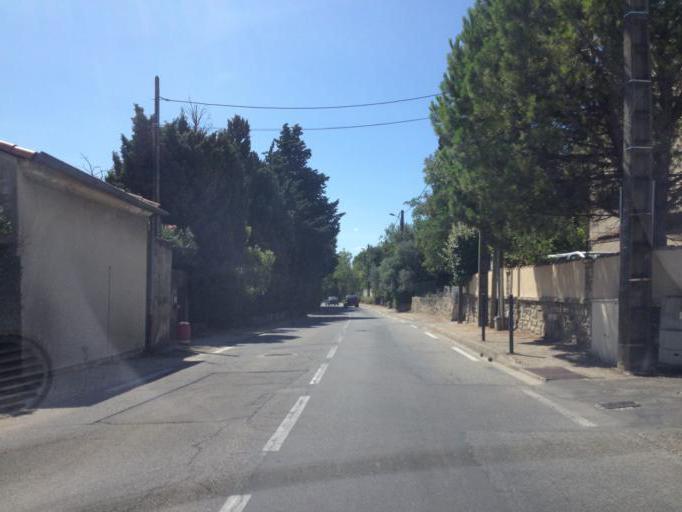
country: FR
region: Languedoc-Roussillon
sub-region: Departement du Gard
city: Villeneuve-les-Avignon
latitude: 43.9748
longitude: 4.7966
